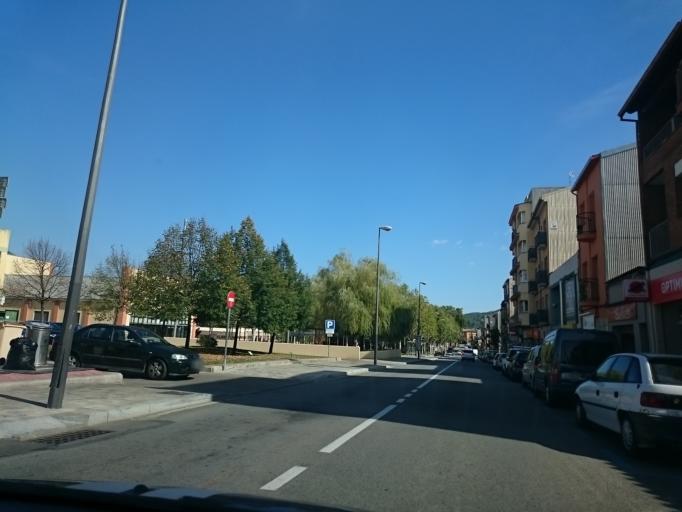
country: ES
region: Catalonia
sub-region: Provincia de Barcelona
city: Llinars del Valles
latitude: 41.6399
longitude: 2.3984
